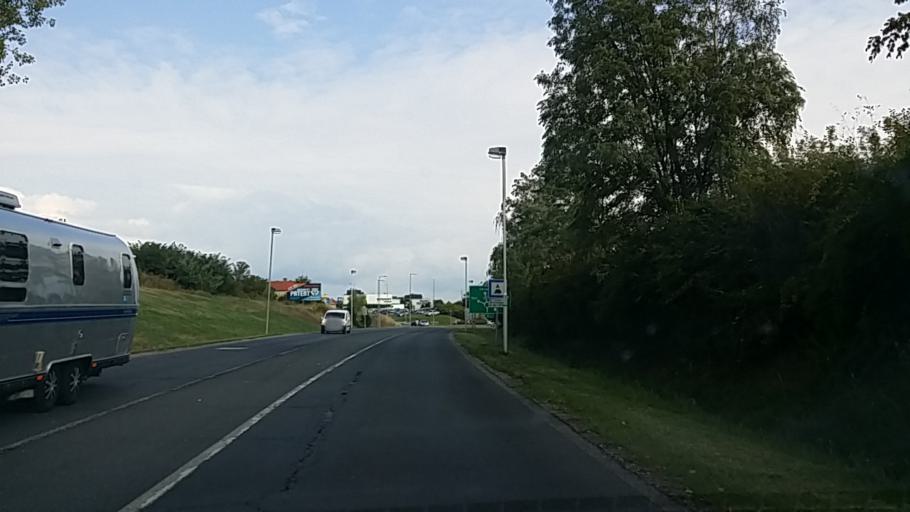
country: HU
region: Gyor-Moson-Sopron
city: Sopron
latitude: 47.6834
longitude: 16.6119
